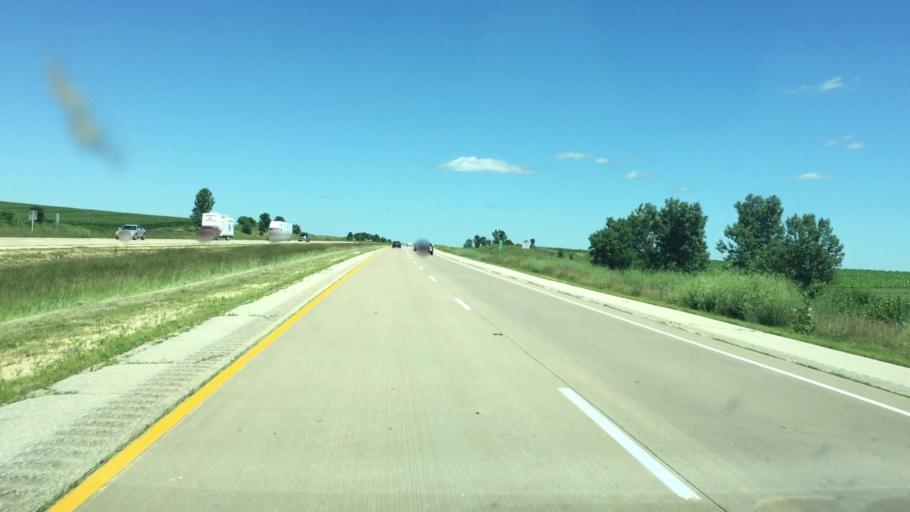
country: US
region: Wisconsin
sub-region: Grant County
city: Platteville
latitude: 42.7400
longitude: -90.3819
